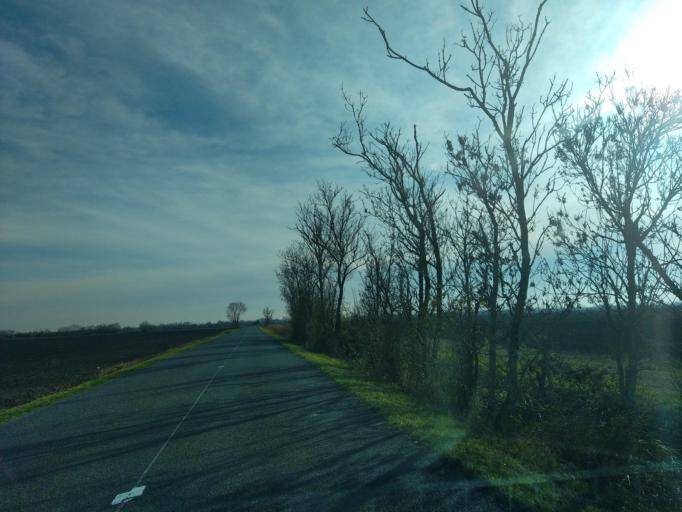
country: FR
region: Pays de la Loire
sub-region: Departement de la Vendee
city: Maillezais
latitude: 46.3821
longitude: -0.7851
